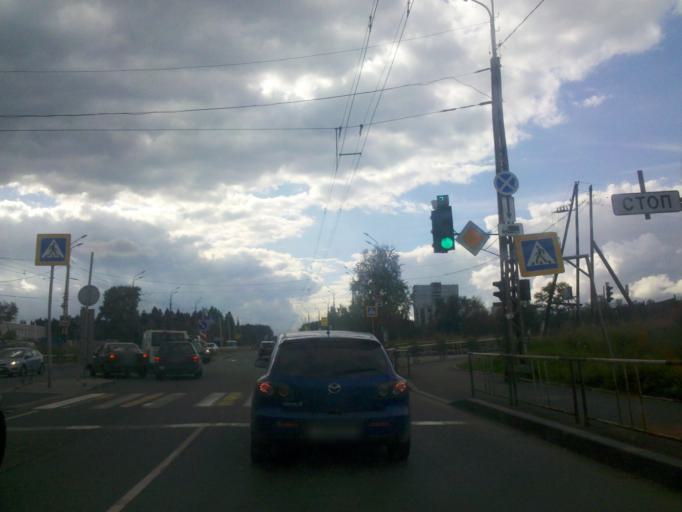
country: RU
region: Republic of Karelia
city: Petrozavodsk
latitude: 61.7822
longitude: 34.3196
